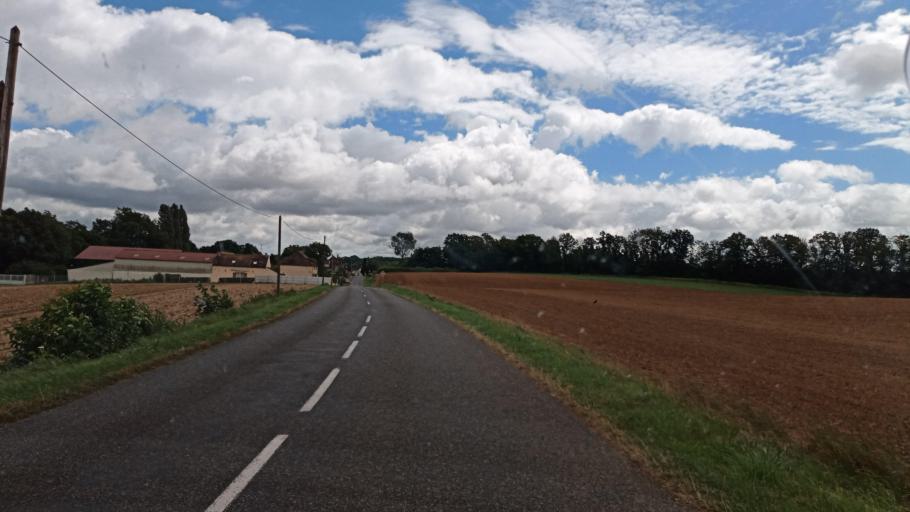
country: FR
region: Bourgogne
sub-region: Departement de l'Yonne
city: Cheroy
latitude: 48.2434
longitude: 3.0387
